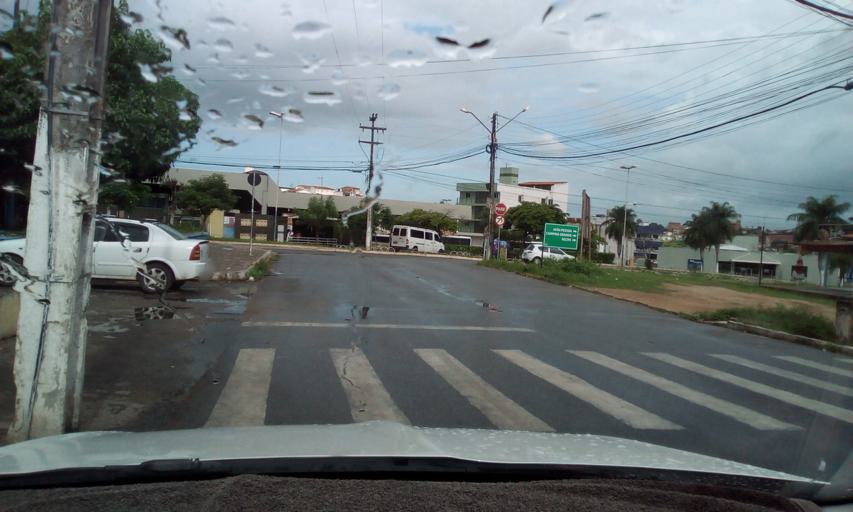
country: BR
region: Paraiba
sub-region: Guarabira
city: Guarabira
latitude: -6.8538
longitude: -35.4967
